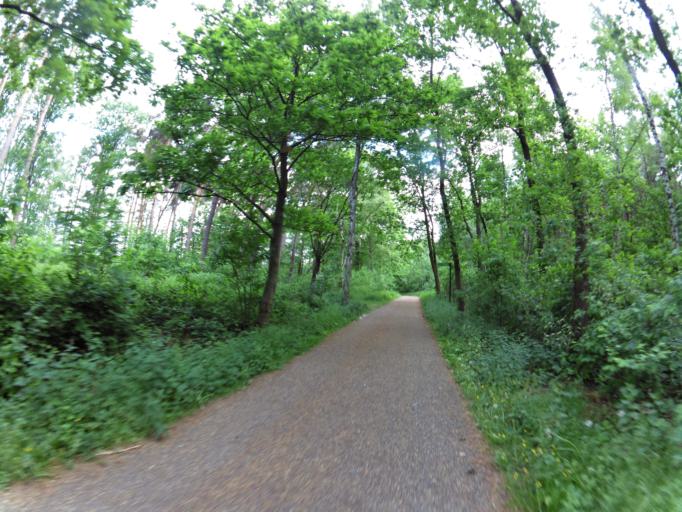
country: NL
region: Limburg
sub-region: Gemeente Brunssum
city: Brunssum
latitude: 50.9519
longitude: 5.9901
